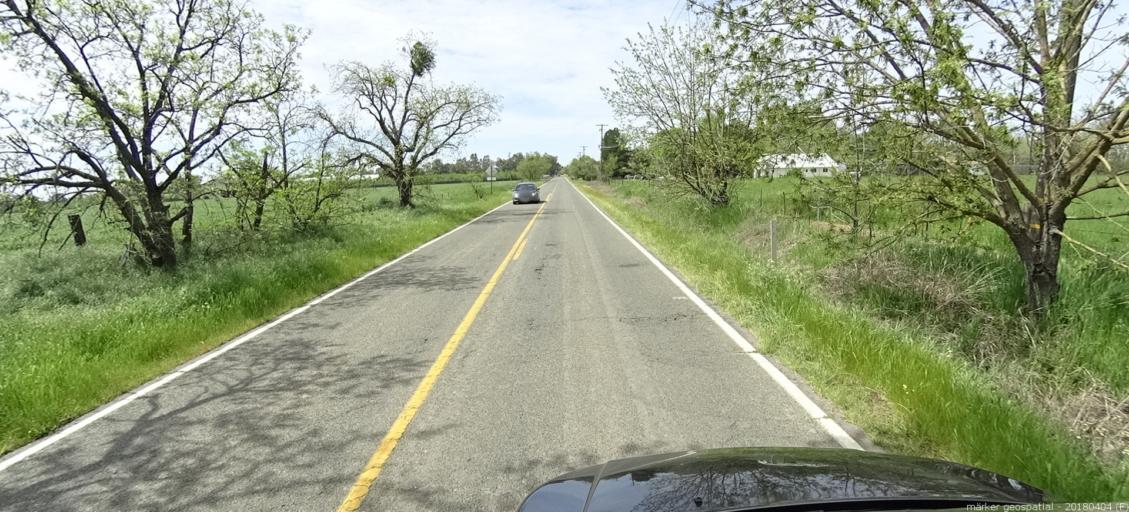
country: US
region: California
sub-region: Sacramento County
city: Herald
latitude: 38.2626
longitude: -121.2551
